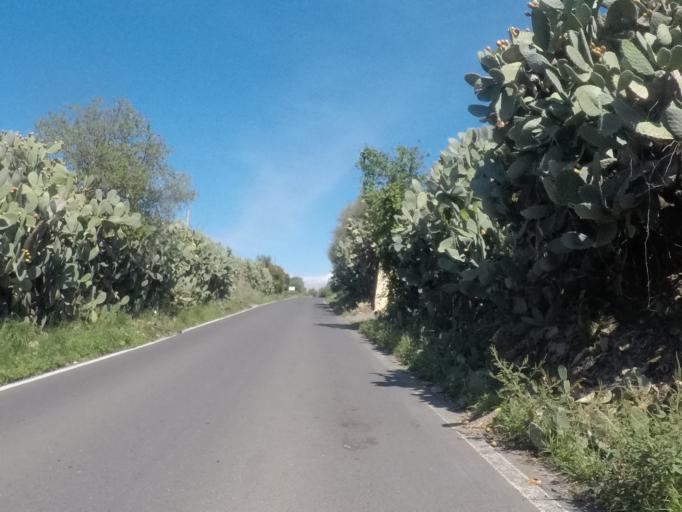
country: IT
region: Sicily
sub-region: Catania
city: Motta Sant'Anastasia
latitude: 37.4885
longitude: 14.9492
